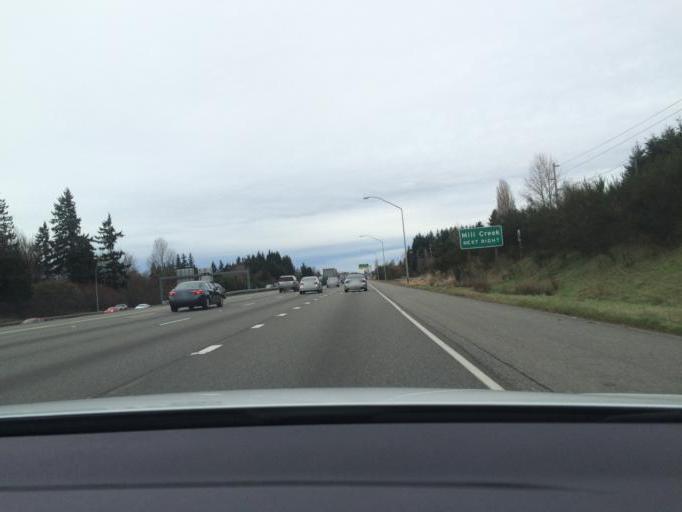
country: US
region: Washington
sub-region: Snohomish County
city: Martha Lake
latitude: 47.8371
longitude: -122.2604
